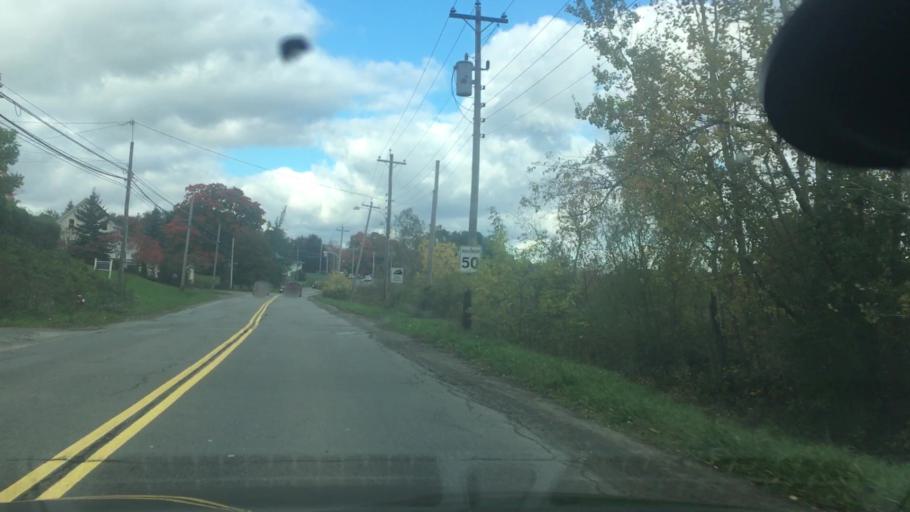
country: CA
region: Nova Scotia
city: Windsor
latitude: 44.9763
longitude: -64.1197
